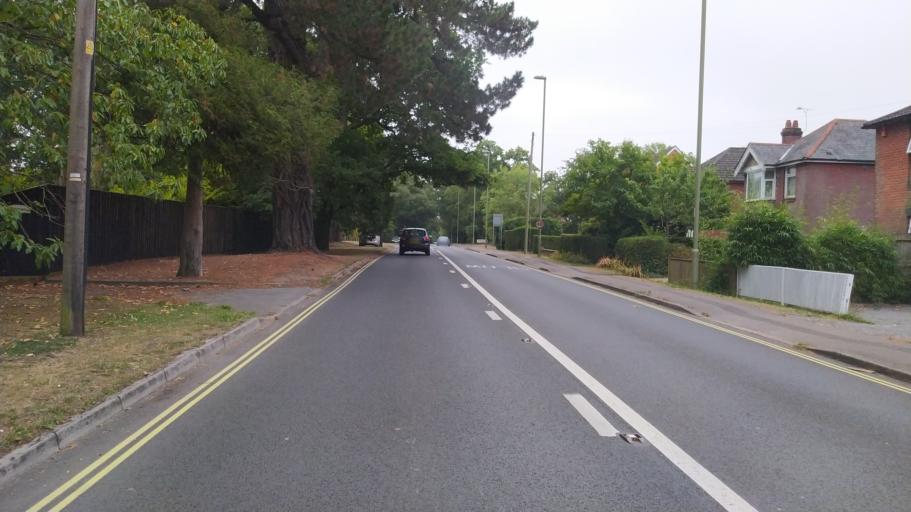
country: GB
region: England
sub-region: Hampshire
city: West End
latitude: 50.9196
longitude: -1.3323
